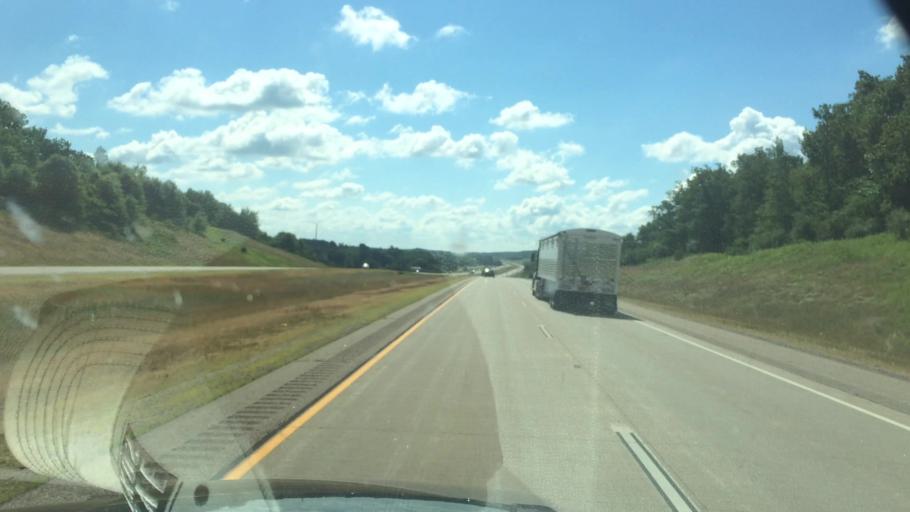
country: US
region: Wisconsin
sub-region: Waupaca County
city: King
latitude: 44.3874
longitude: -89.1881
